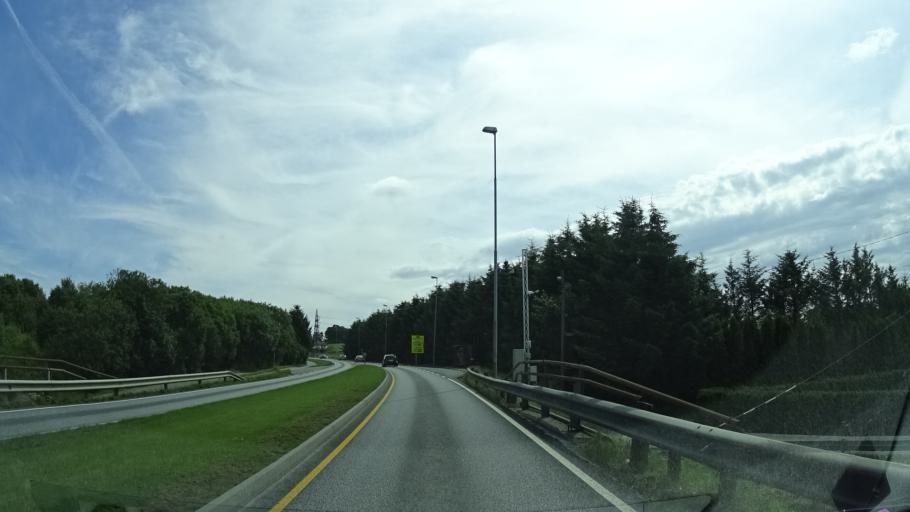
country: NO
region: Rogaland
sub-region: Randaberg
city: Randaberg
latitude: 58.9911
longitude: 5.6540
